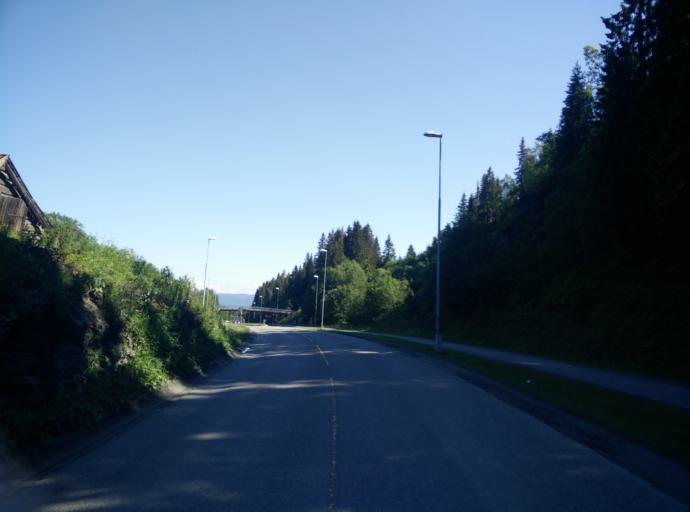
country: NO
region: Sor-Trondelag
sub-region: Trondheim
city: Trondheim
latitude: 63.3764
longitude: 10.3199
